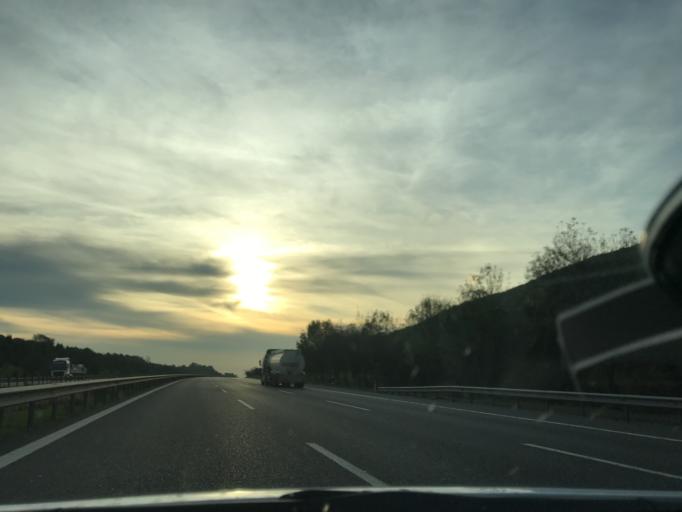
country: TR
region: Duzce
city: Gumusova
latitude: 40.8149
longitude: 30.9078
